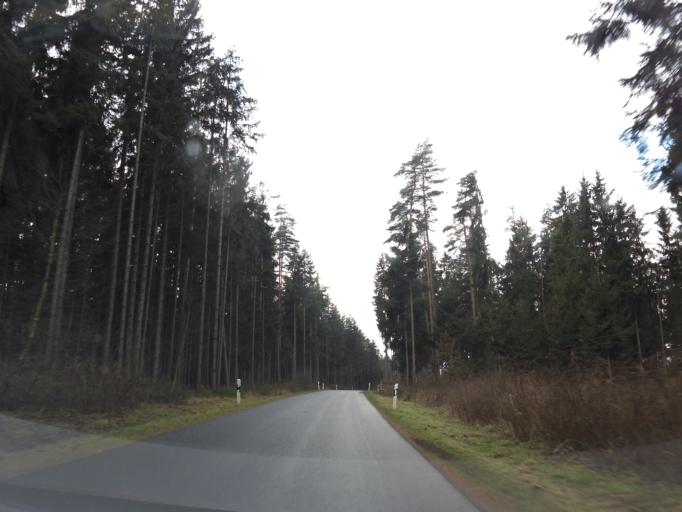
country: DE
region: Bavaria
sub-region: Upper Franconia
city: Wunsiedel
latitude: 50.0692
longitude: 12.0363
